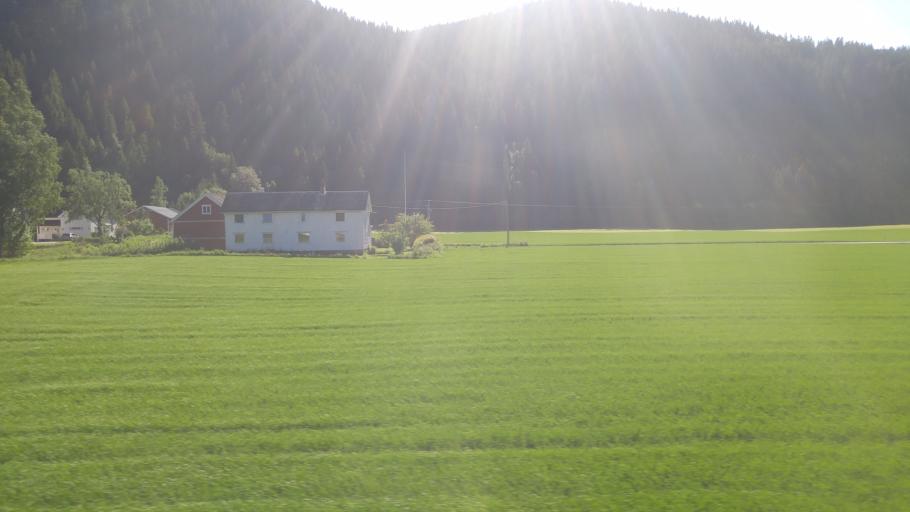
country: NO
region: Sor-Trondelag
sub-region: Midtre Gauldal
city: Storen
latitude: 63.0767
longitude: 10.2533
